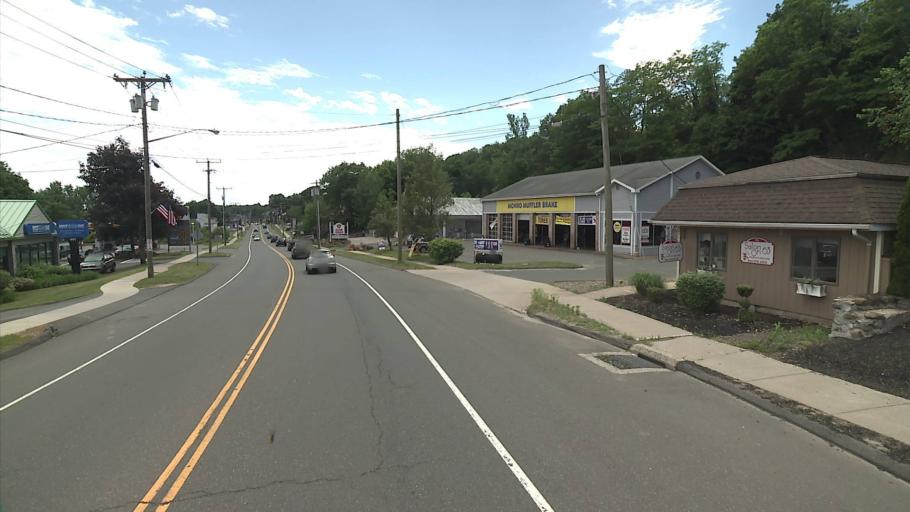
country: US
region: Connecticut
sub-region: Litchfield County
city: Watertown
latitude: 41.5970
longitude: -73.1134
